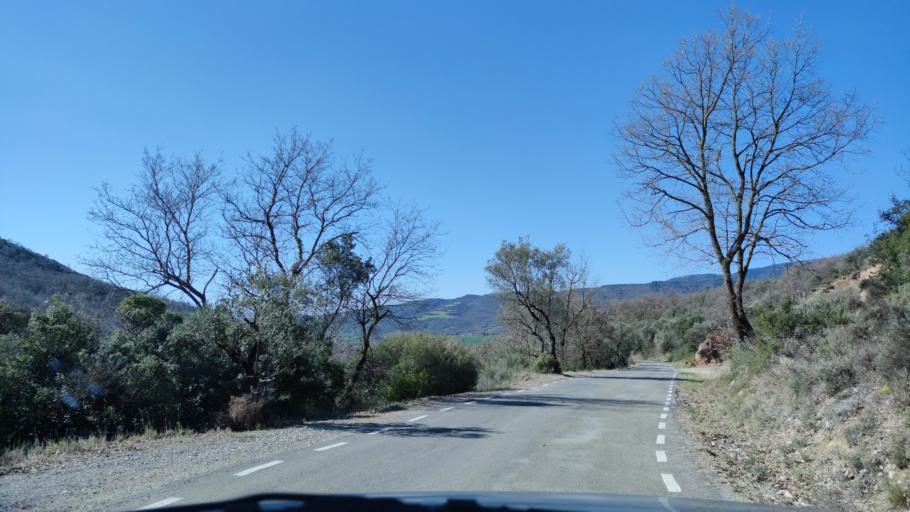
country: ES
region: Catalonia
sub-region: Provincia de Lleida
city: Artesa de Segre
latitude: 42.0030
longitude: 1.0293
